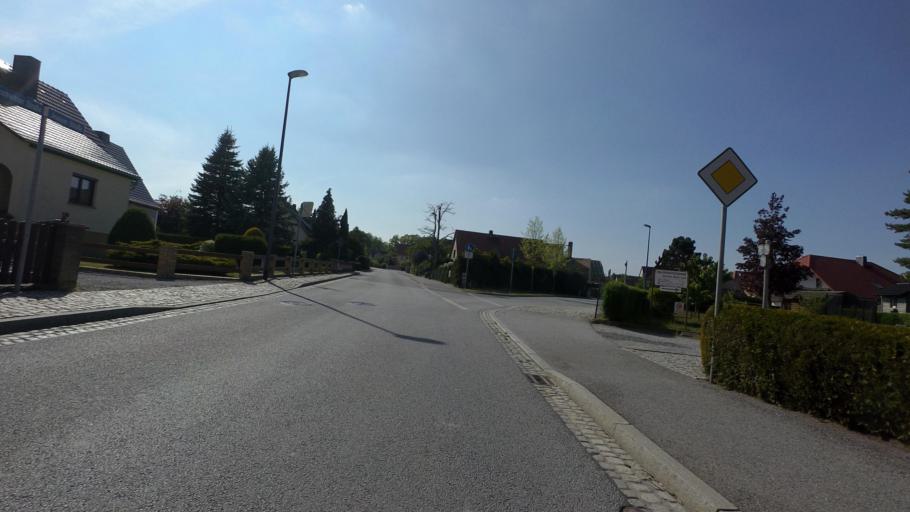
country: DE
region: Saxony
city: Kamenz
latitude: 51.2823
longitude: 14.1233
